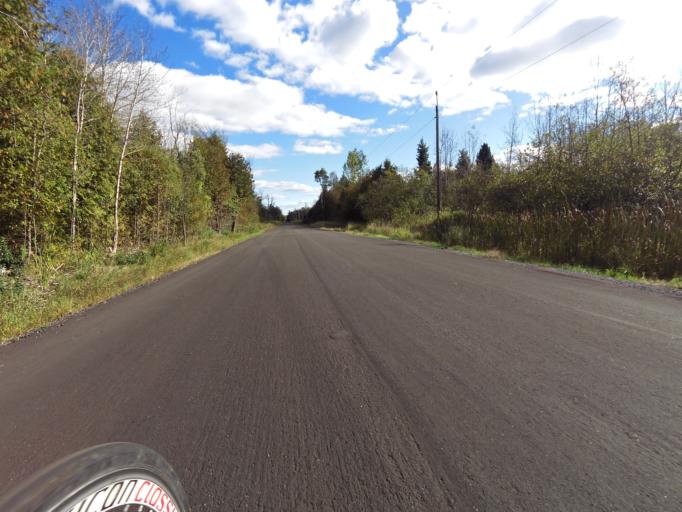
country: CA
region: Ontario
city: Bells Corners
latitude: 45.1041
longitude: -75.6481
